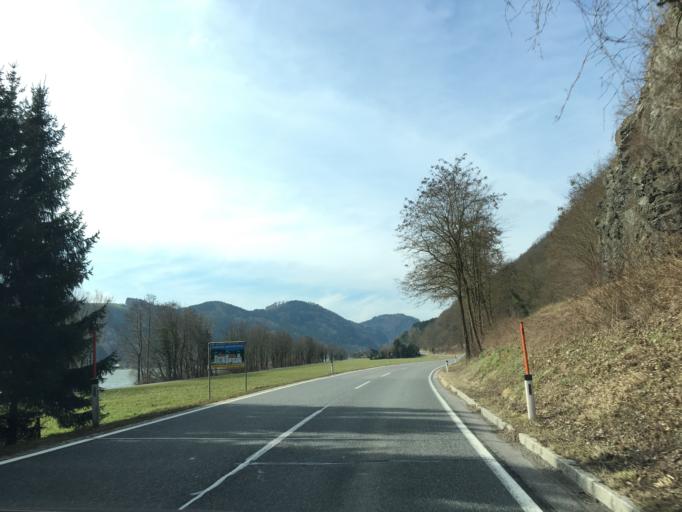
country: AT
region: Lower Austria
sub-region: Politischer Bezirk Melk
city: Nochling
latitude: 48.1973
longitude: 14.9927
